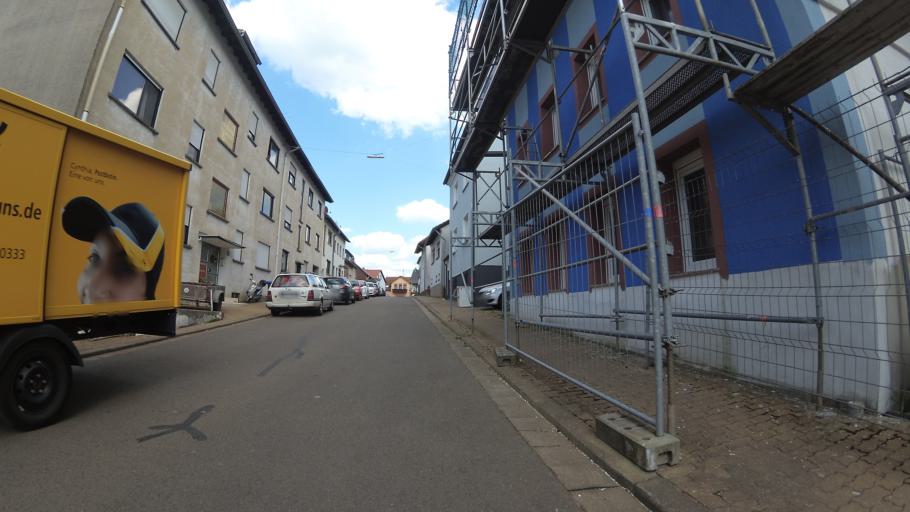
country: DE
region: Saarland
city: Riegelsberg
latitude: 49.3055
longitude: 6.9428
